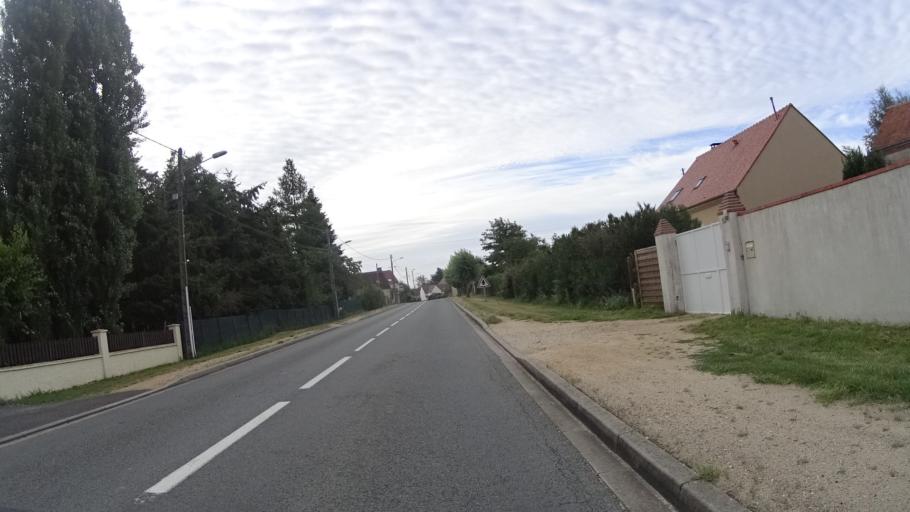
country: FR
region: Centre
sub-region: Departement du Loiret
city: Chateauneuf-sur-Loire
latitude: 47.8475
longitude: 2.2619
